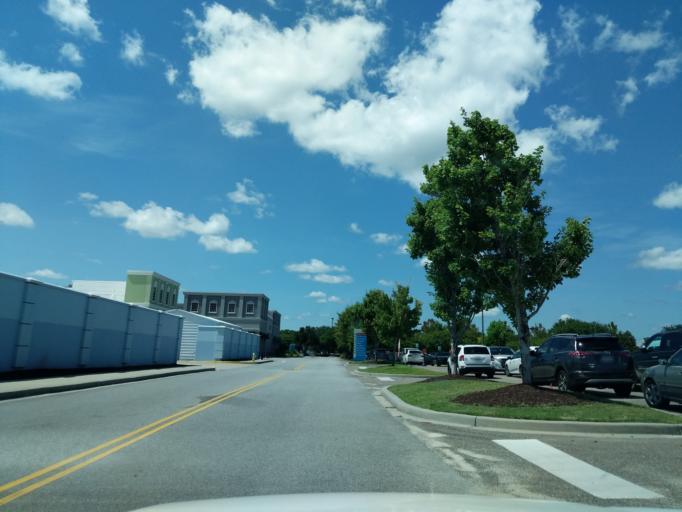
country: US
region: South Carolina
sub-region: Berkeley County
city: Hanahan
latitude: 32.8741
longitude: -80.0177
